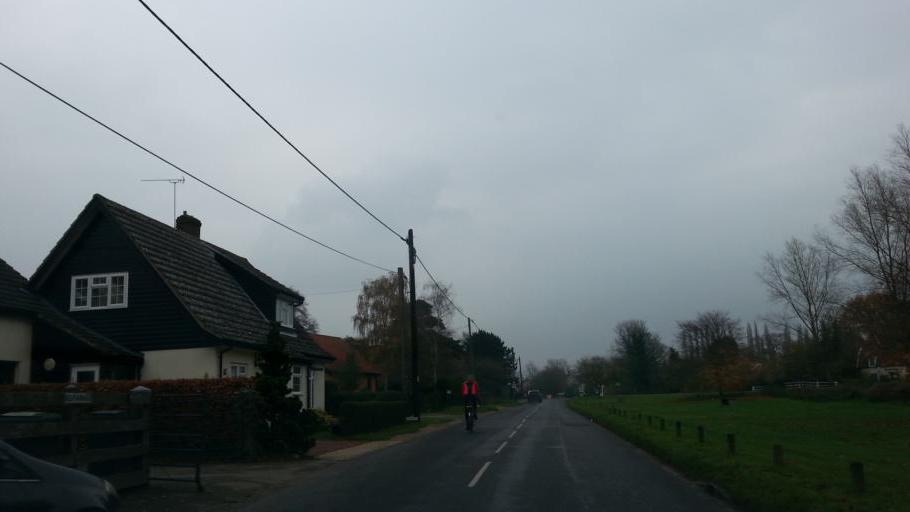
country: GB
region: England
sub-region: Suffolk
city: Thurston
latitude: 52.2351
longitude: 0.8322
